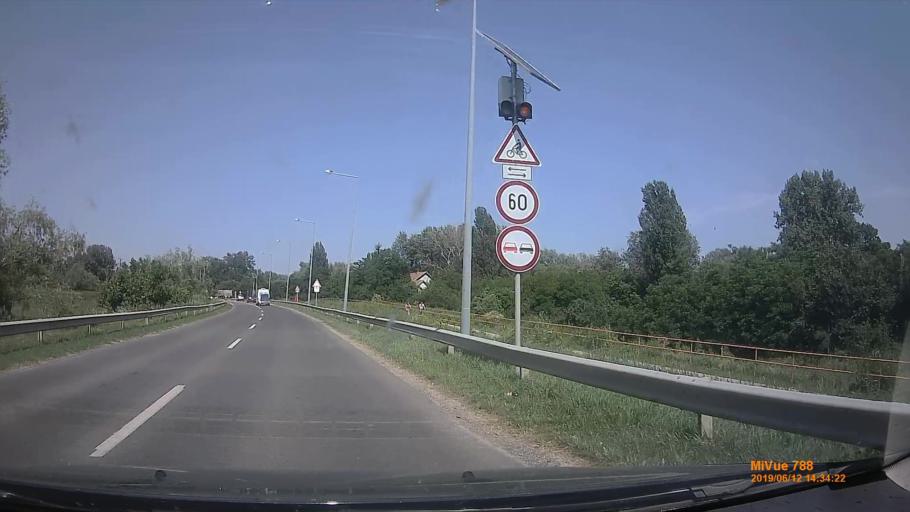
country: HU
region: Csongrad
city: Kiszombor
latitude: 46.1995
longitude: 20.4497
